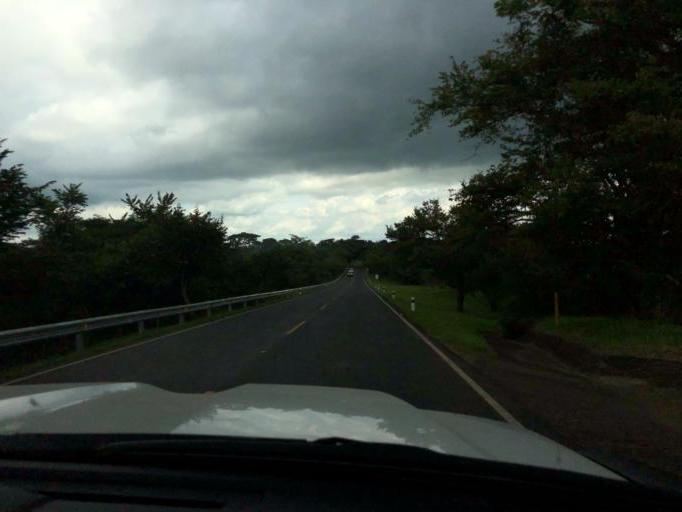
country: NI
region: Chontales
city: Villa Sandino
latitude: 12.0597
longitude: -85.0098
